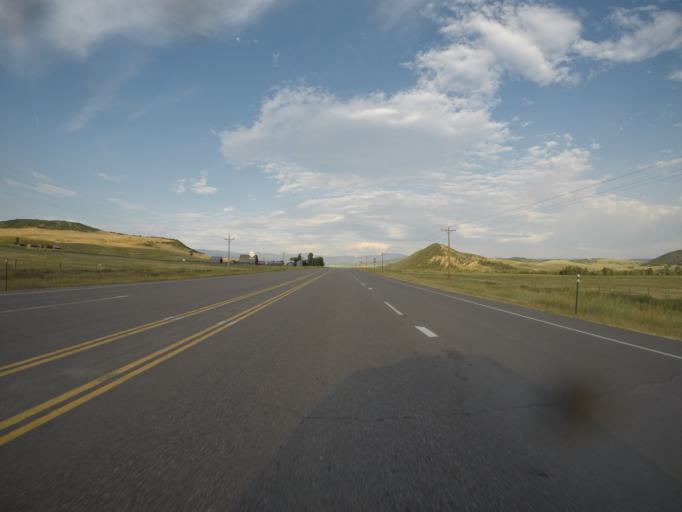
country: US
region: Colorado
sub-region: Routt County
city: Steamboat Springs
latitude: 40.4857
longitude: -107.0100
